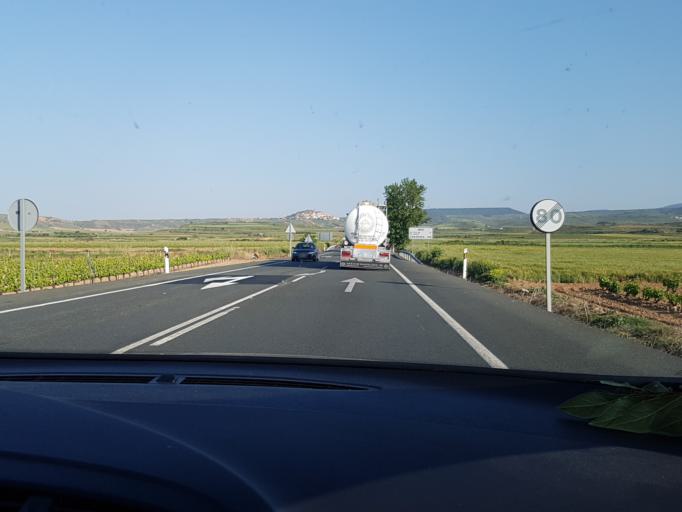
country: ES
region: La Rioja
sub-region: Provincia de La Rioja
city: Corera
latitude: 42.3764
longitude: -2.2028
